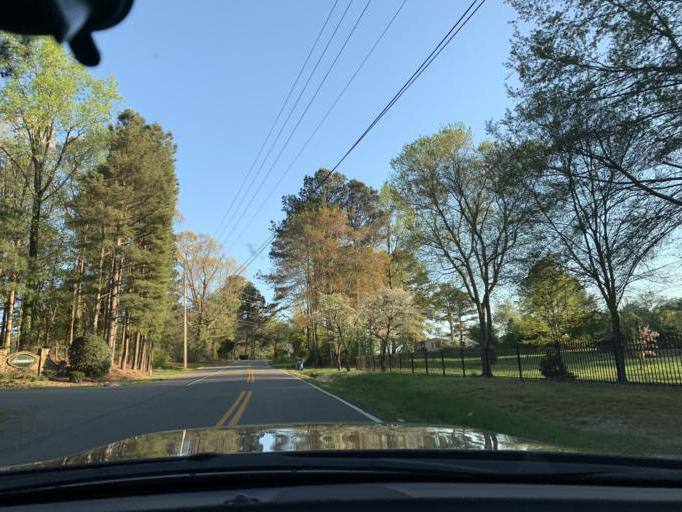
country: US
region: Georgia
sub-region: Forsyth County
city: Cumming
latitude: 34.2367
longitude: -84.2144
